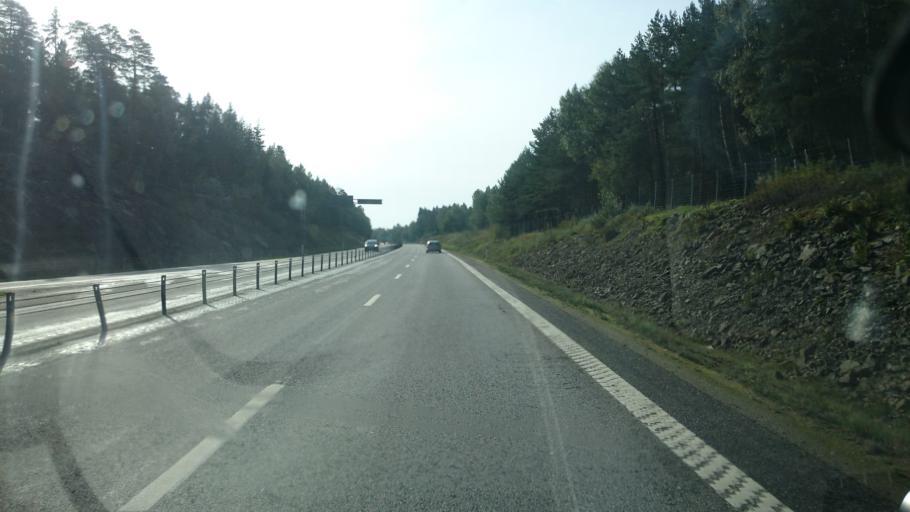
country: SE
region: Vaestra Goetaland
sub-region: Trollhattan
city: Trollhattan
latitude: 58.3308
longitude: 12.2978
